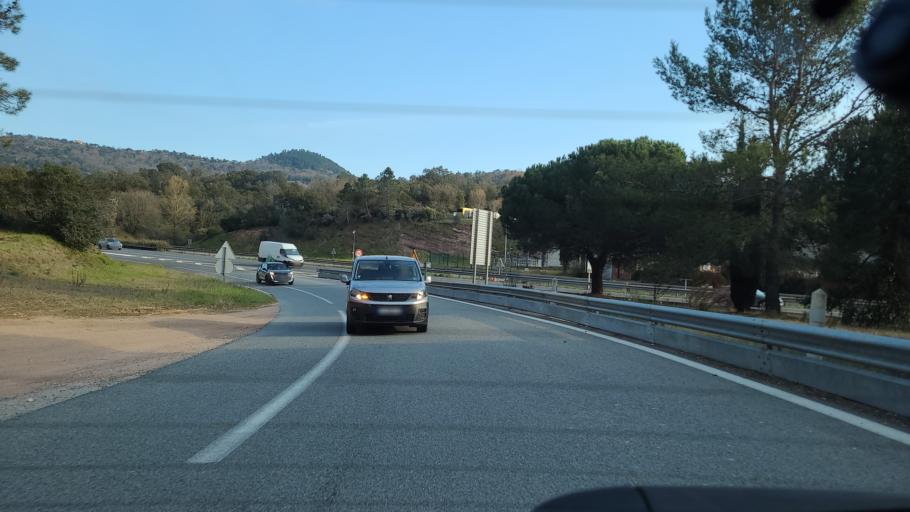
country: FR
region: Provence-Alpes-Cote d'Azur
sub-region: Departement du Var
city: Tanneron
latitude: 43.5449
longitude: 6.8123
